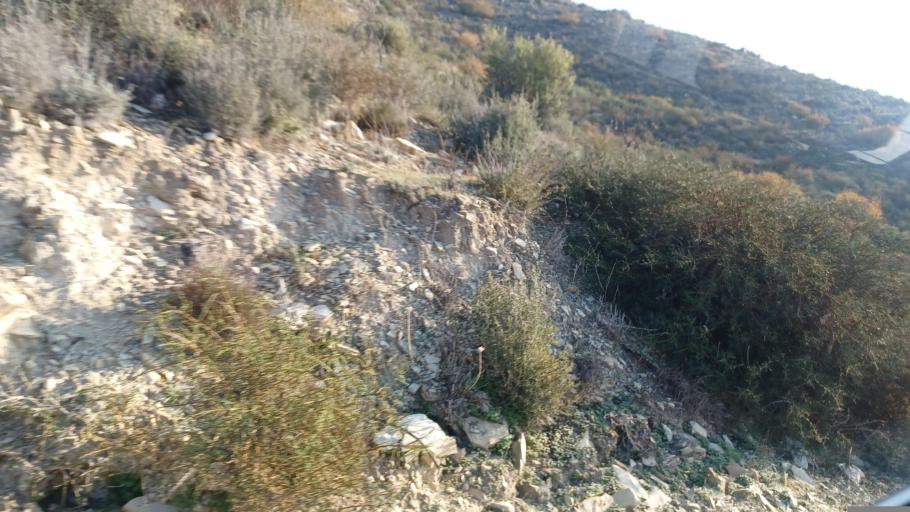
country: CY
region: Larnaka
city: Kofinou
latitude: 34.8244
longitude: 33.3095
